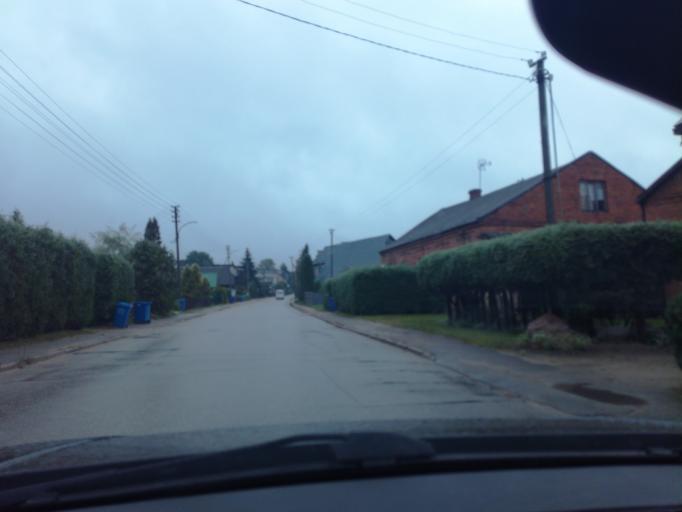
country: LT
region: Alytaus apskritis
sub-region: Alytus
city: Alytus
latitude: 54.4022
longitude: 24.0667
